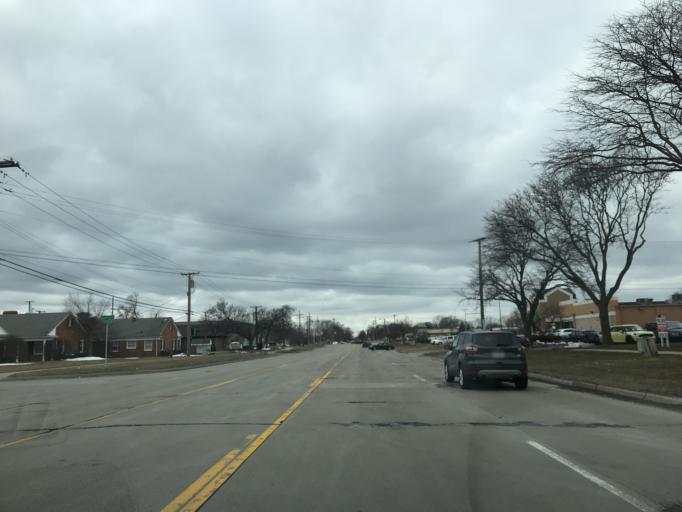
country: US
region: Michigan
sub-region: Oakland County
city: Bingham Farms
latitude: 42.4871
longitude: -83.2573
